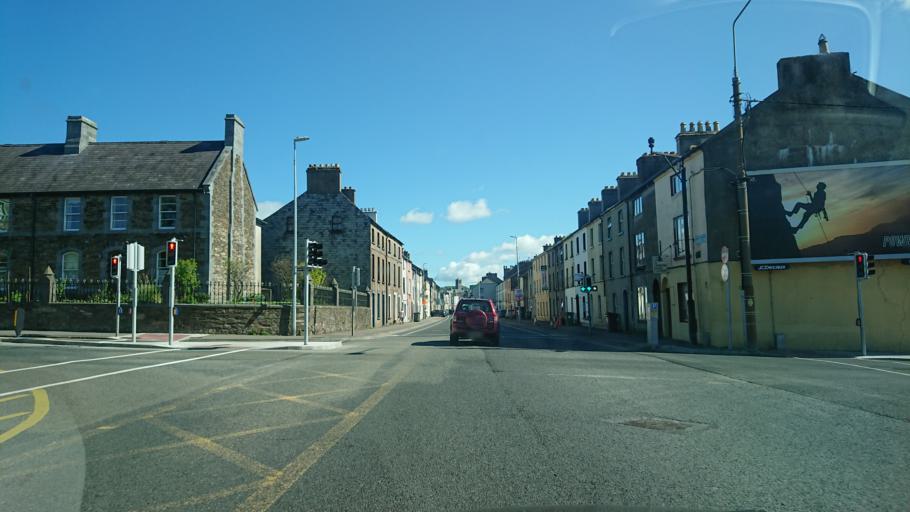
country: IE
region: Munster
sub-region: Waterford
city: Waterford
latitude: 52.2542
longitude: -7.1144
